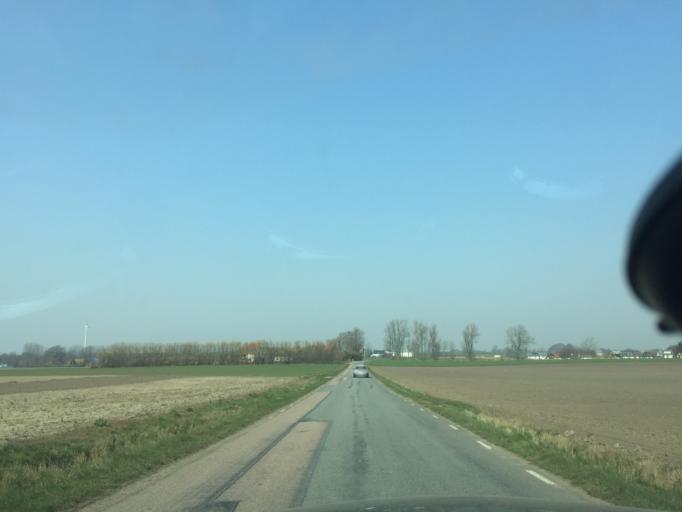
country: SE
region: Skane
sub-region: Simrishamns Kommun
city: Simrishamn
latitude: 55.4626
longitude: 14.2100
